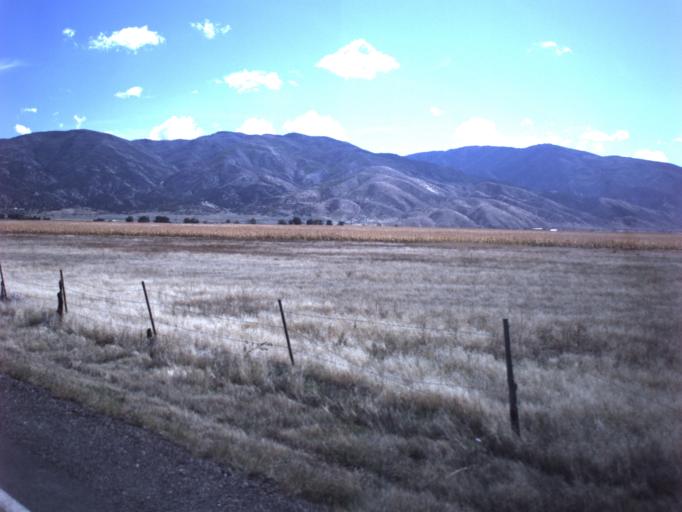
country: US
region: Utah
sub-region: Juab County
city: Nephi
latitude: 39.5579
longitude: -111.9004
